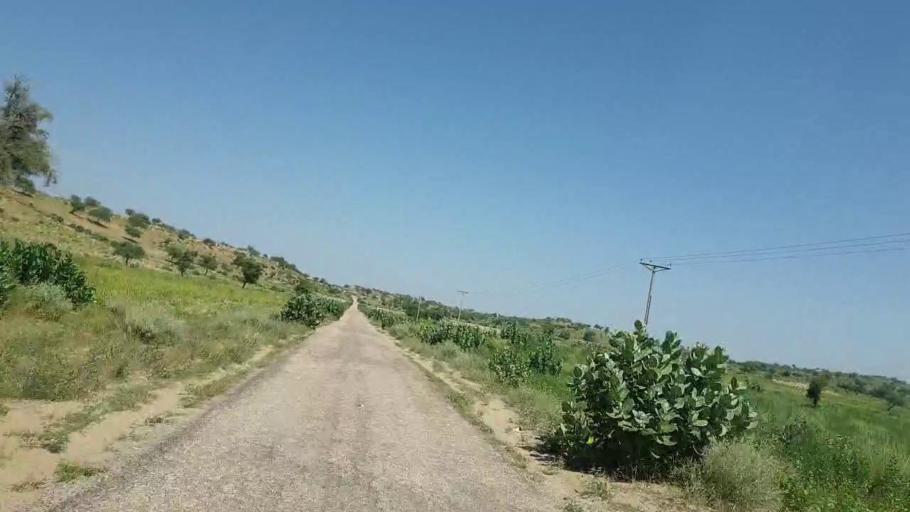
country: PK
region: Sindh
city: Islamkot
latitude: 25.1693
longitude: 70.4174
